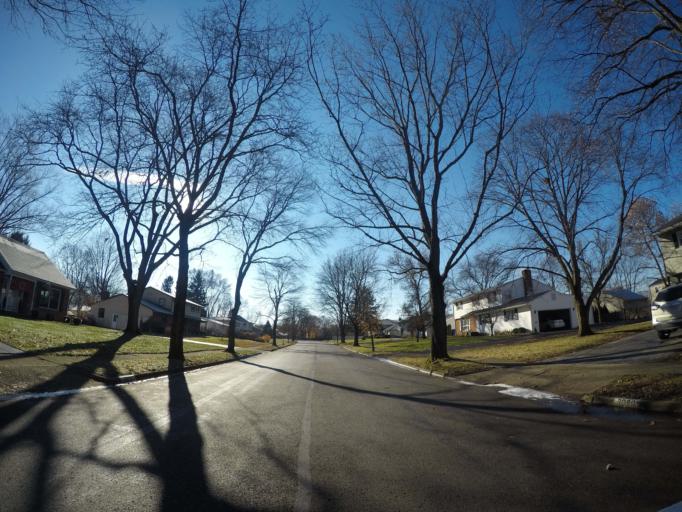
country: US
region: Ohio
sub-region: Franklin County
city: Upper Arlington
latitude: 40.0366
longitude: -83.0655
